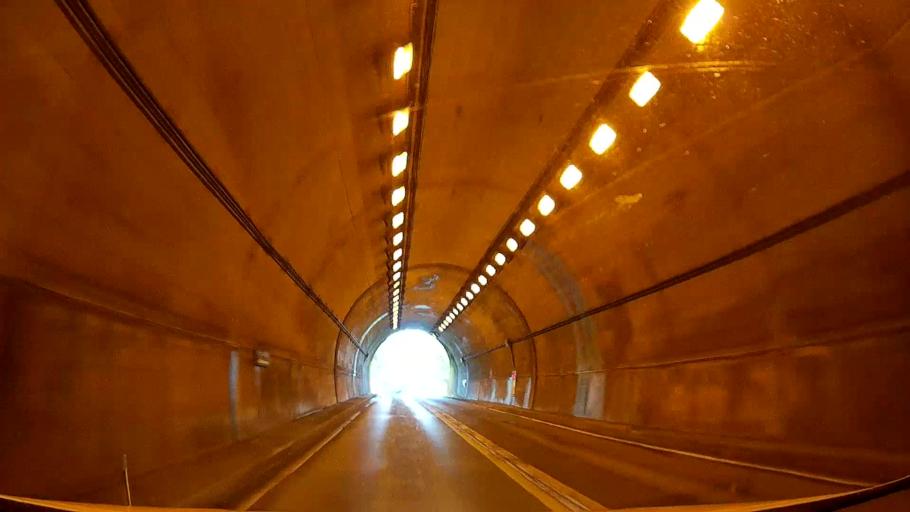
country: JP
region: Shizuoka
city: Heda
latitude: 34.9209
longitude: 138.8475
